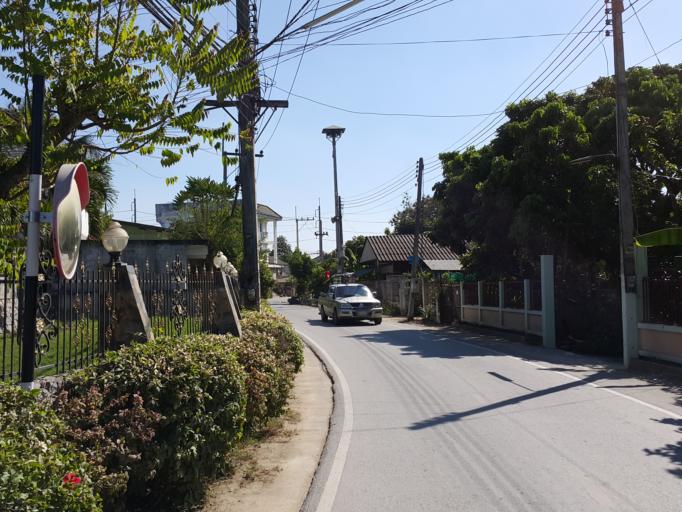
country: TH
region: Chiang Mai
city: Saraphi
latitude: 18.7406
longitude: 99.0435
